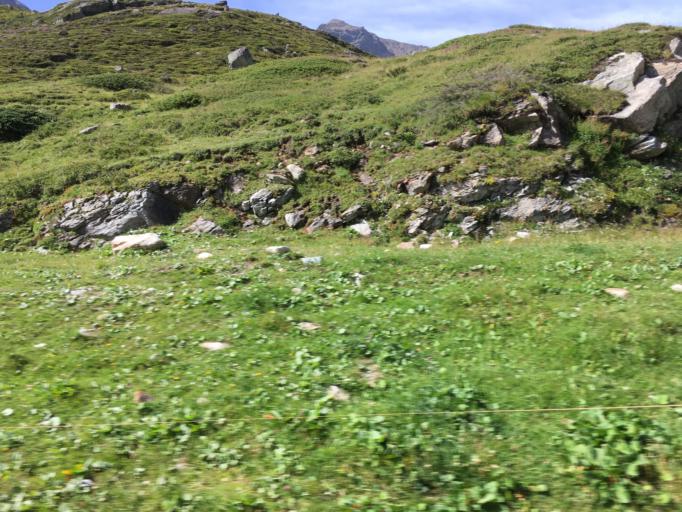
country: CH
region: Grisons
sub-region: Maloja District
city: Silvaplana
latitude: 46.4665
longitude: 9.6965
